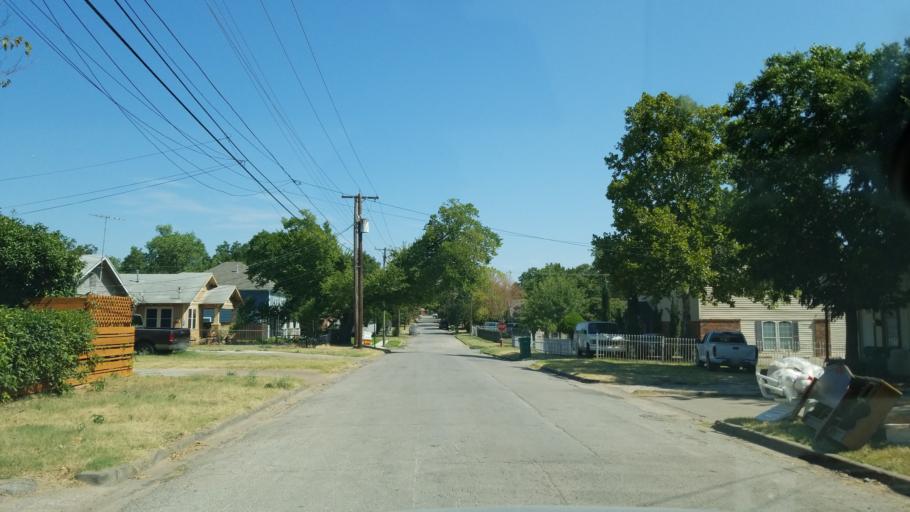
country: US
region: Texas
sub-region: Dallas County
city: Cockrell Hill
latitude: 32.7392
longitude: -96.8900
